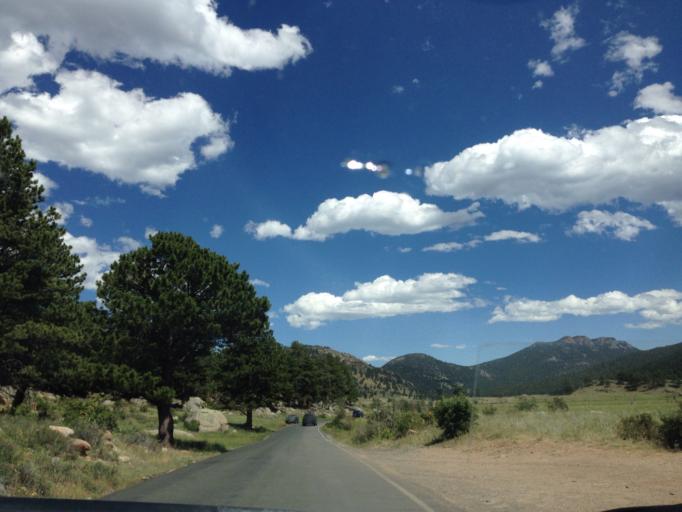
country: US
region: Colorado
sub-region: Larimer County
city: Estes Park
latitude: 40.3569
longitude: -105.6079
